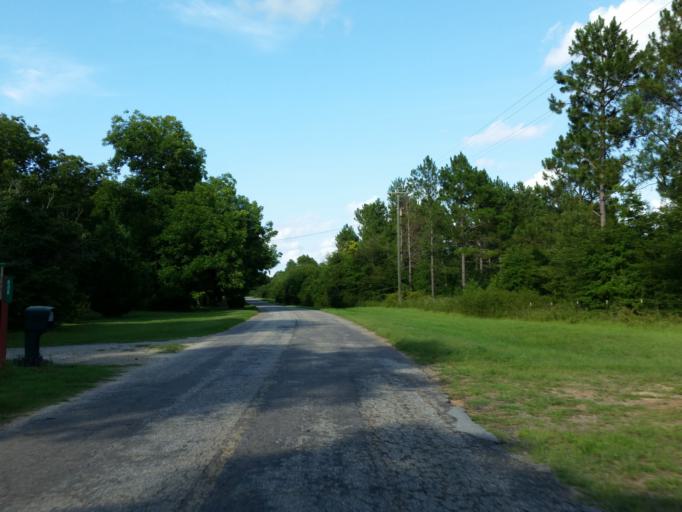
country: US
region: Georgia
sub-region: Lee County
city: Leesburg
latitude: 31.9134
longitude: -84.0185
